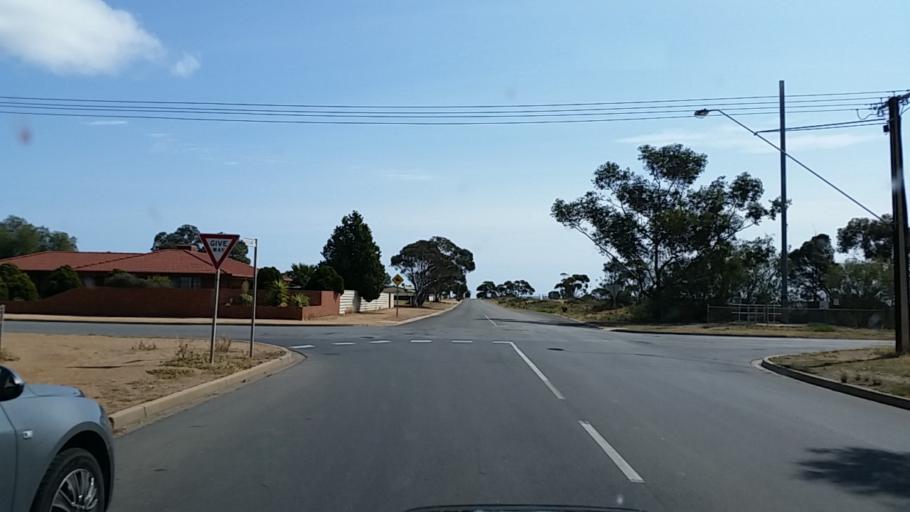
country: AU
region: South Australia
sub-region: Port Pirie City and Dists
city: Port Pirie
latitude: -33.1893
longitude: 137.9916
